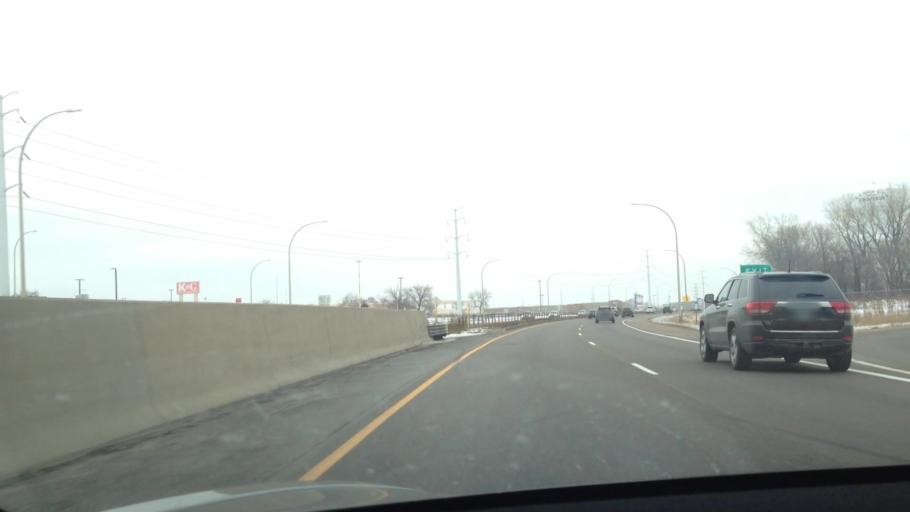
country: US
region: Minnesota
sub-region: Hennepin County
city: Robbinsdale
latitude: 45.0510
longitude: -93.3221
